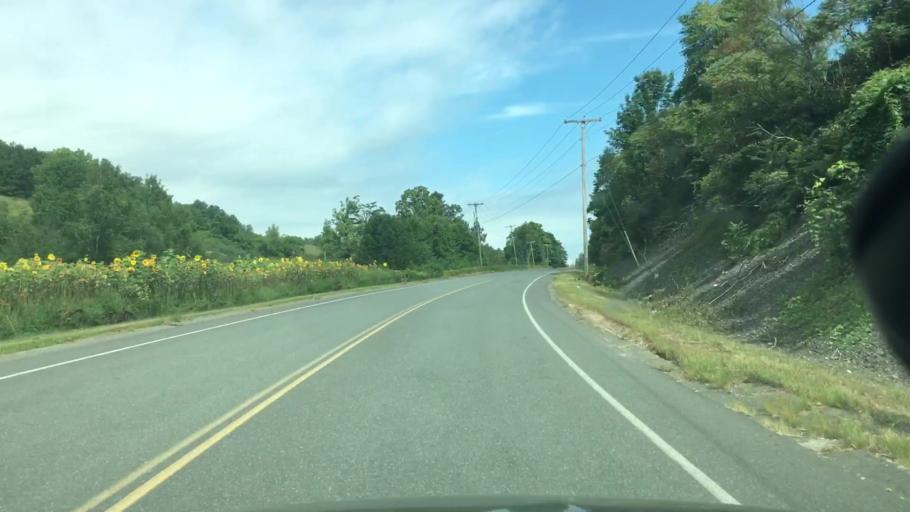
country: US
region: Massachusetts
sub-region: Franklin County
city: Colrain
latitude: 42.6434
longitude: -72.6745
